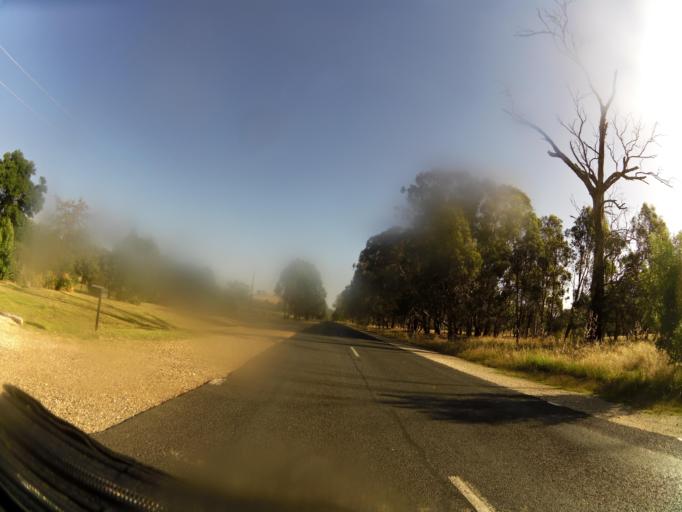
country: AU
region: Victoria
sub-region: Murrindindi
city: Kinglake West
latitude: -36.9933
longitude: 145.1127
